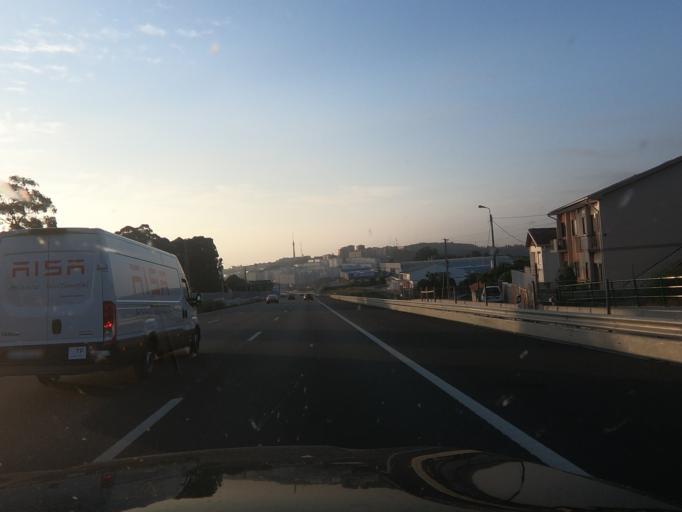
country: PT
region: Porto
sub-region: Vila Nova de Gaia
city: Canelas
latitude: 41.0850
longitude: -8.5841
